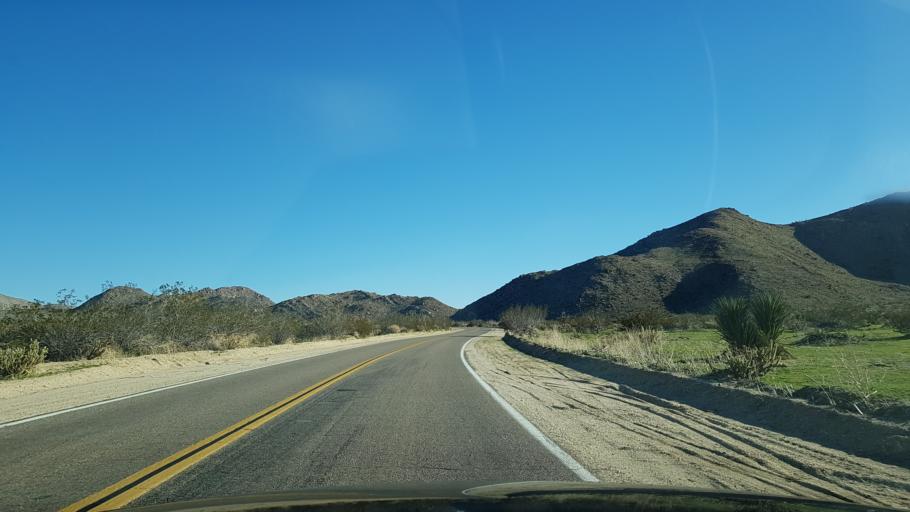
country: US
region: California
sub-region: San Diego County
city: Julian
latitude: 33.0504
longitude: -116.4166
